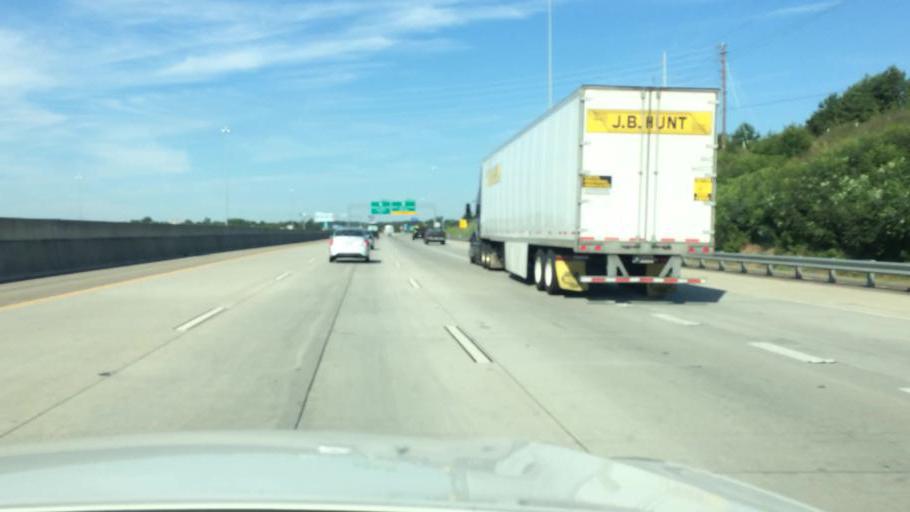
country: US
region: Georgia
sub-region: Columbia County
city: Martinez
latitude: 33.5242
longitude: -82.0256
